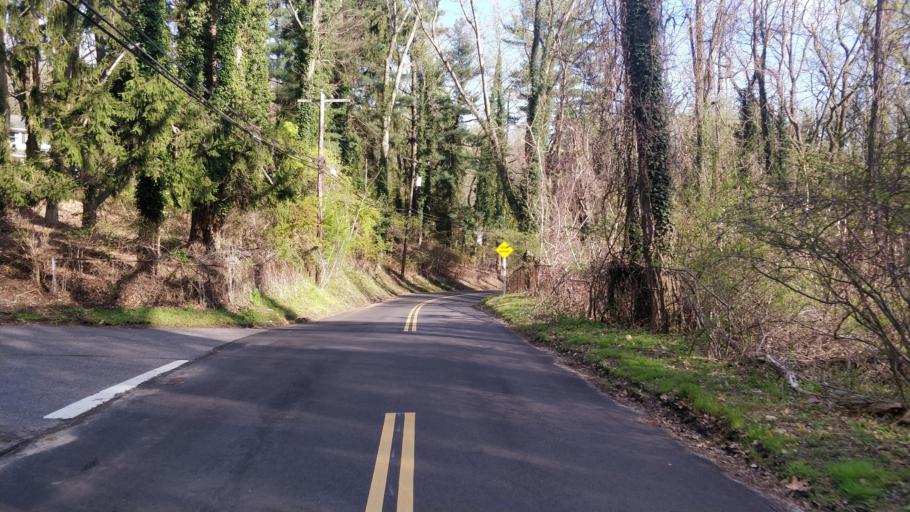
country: US
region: New York
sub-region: Suffolk County
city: Head of the Harbor
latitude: 40.8955
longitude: -73.1667
